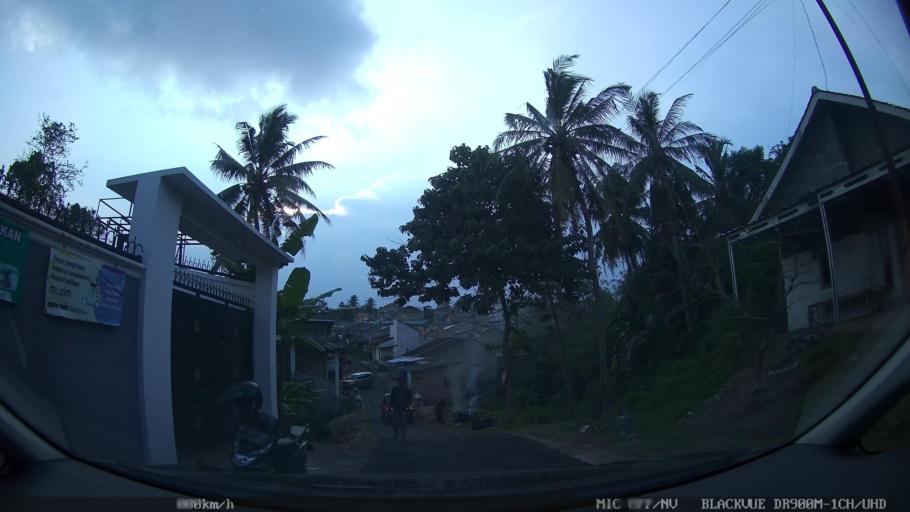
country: ID
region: Lampung
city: Kedaton
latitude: -5.4028
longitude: 105.2956
